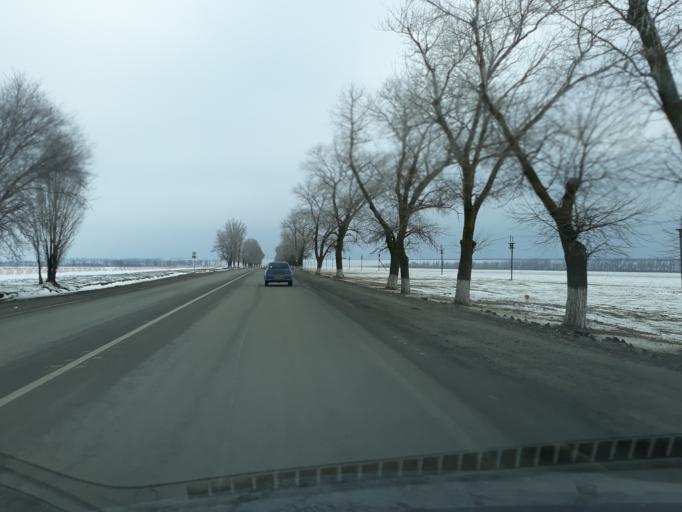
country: RU
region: Rostov
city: Primorka
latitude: 47.3193
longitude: 39.0916
